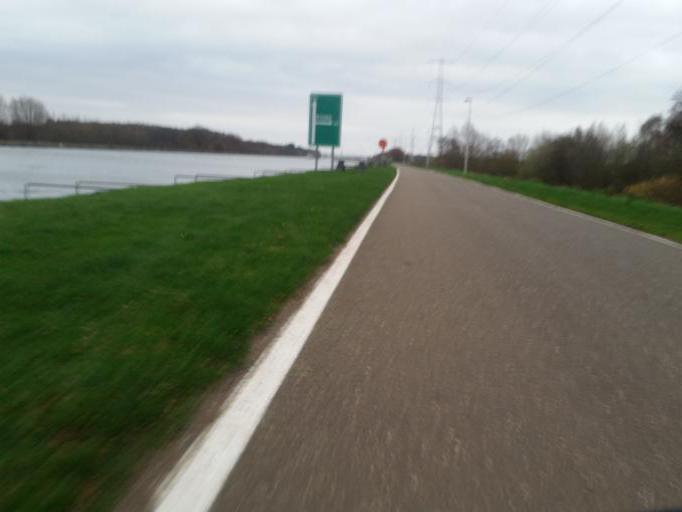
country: BE
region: Flanders
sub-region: Provincie Antwerpen
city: Zandhoven
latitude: 51.1909
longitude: 4.6629
